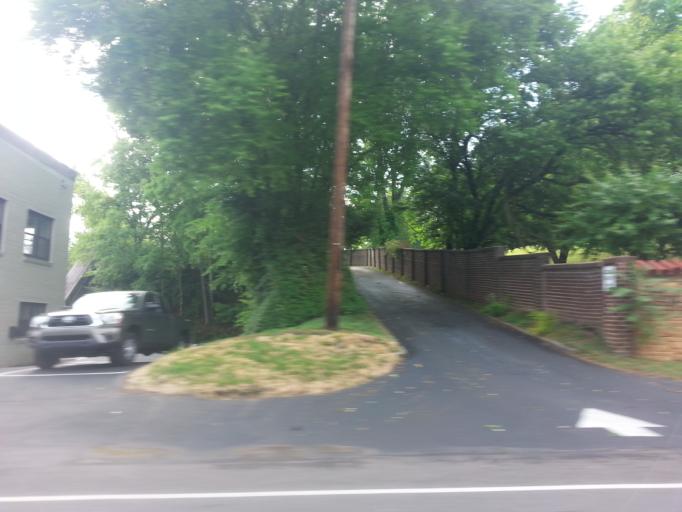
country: US
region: Tennessee
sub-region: Knox County
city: Knoxville
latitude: 35.9279
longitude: -83.9914
